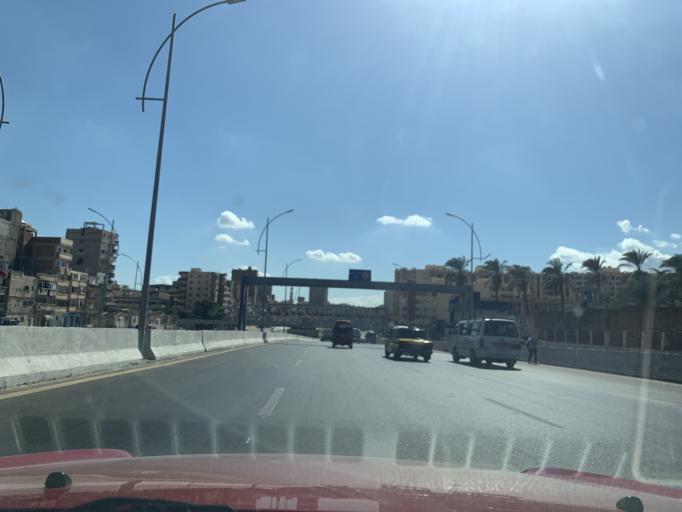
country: EG
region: Alexandria
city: Alexandria
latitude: 31.2191
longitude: 29.9640
